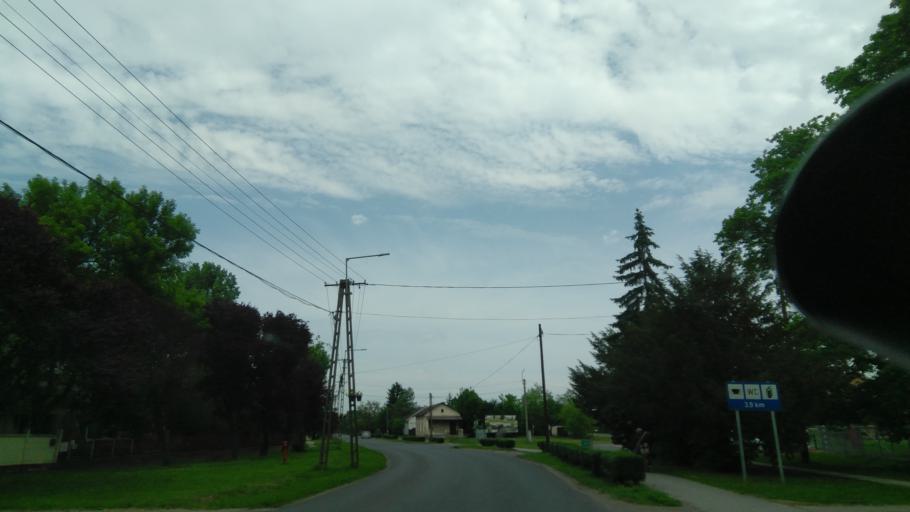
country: HU
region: Bekes
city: Fuzesgyarmat
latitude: 47.0963
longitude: 21.2068
